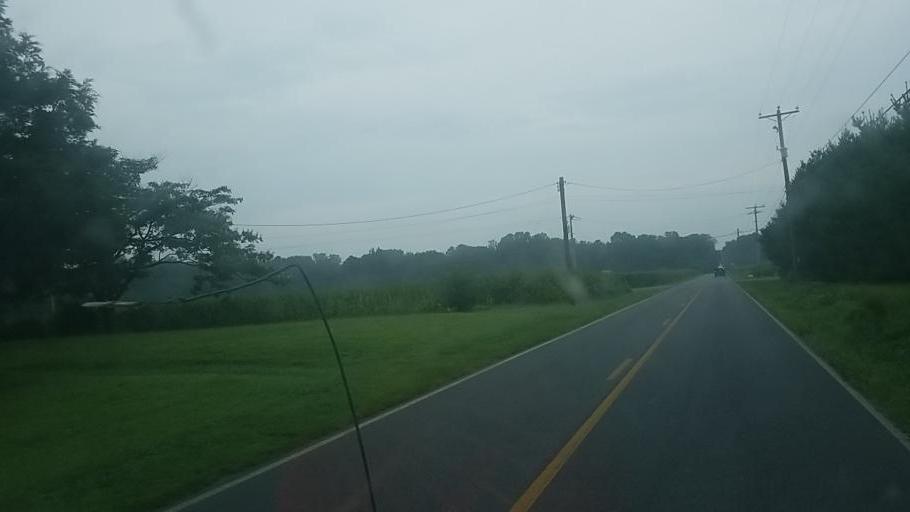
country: US
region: Maryland
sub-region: Wicomico County
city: Salisbury
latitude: 38.3907
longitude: -75.5302
